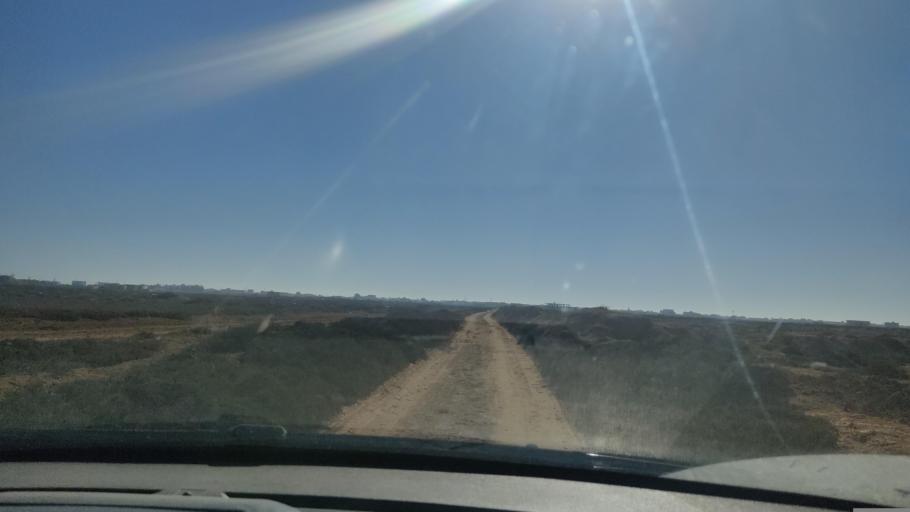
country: TN
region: Safaqis
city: Al Qarmadah
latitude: 34.8165
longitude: 10.8555
